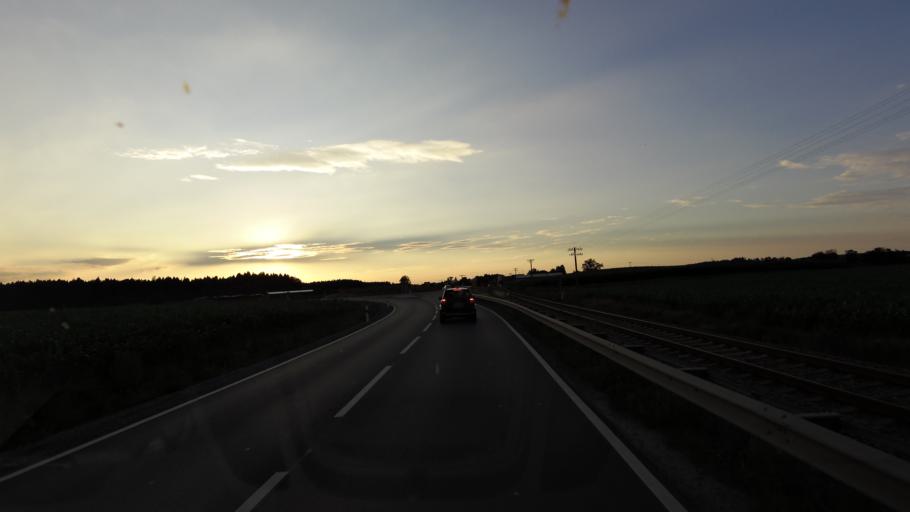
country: DE
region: Bavaria
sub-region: Upper Bavaria
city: Nussdorf
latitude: 47.9313
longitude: 12.5983
